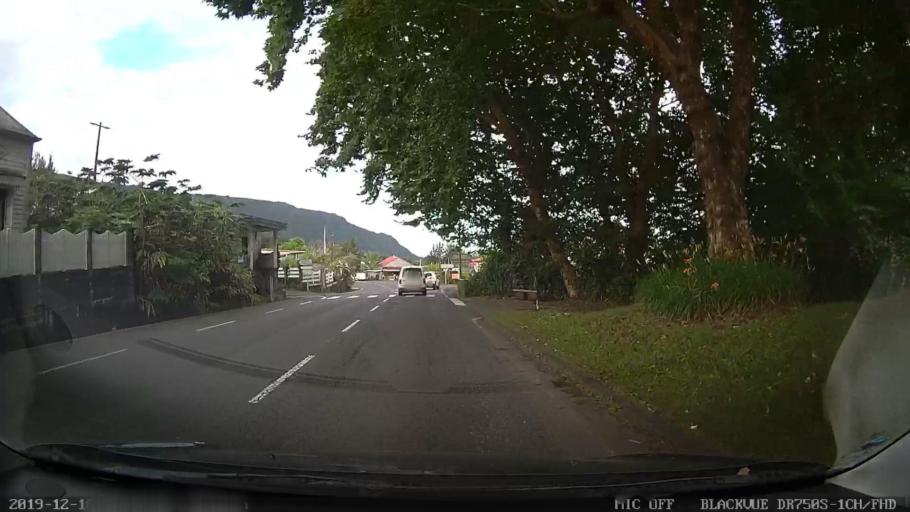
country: RE
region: Reunion
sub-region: Reunion
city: Salazie
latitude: -21.1408
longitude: 55.6223
